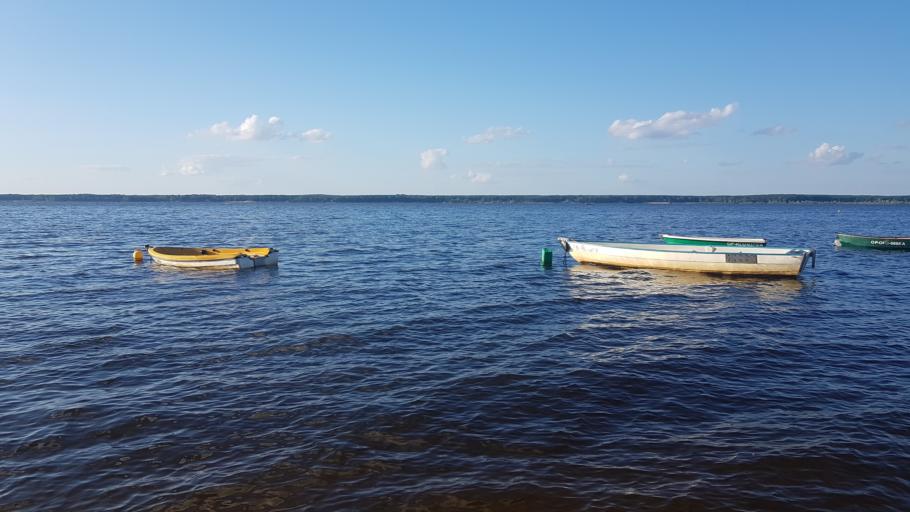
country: PL
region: Opole Voivodeship
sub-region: Powiat opolski
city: Chrzastowice
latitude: 50.7100
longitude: 18.1224
